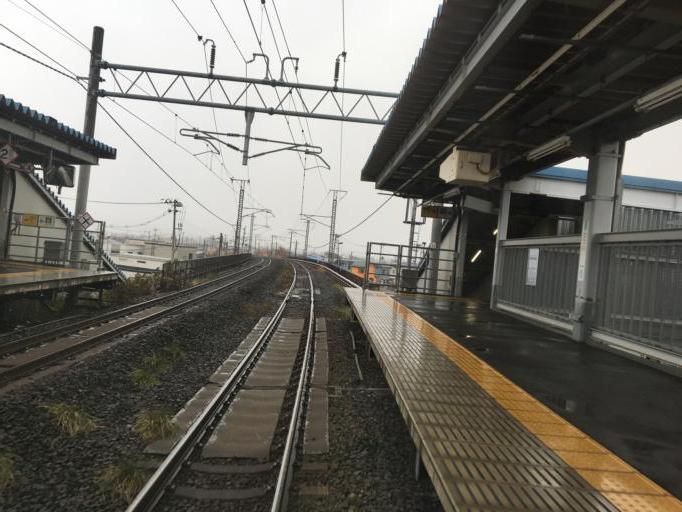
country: JP
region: Aomori
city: Aomori Shi
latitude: 40.8057
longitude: 140.7696
